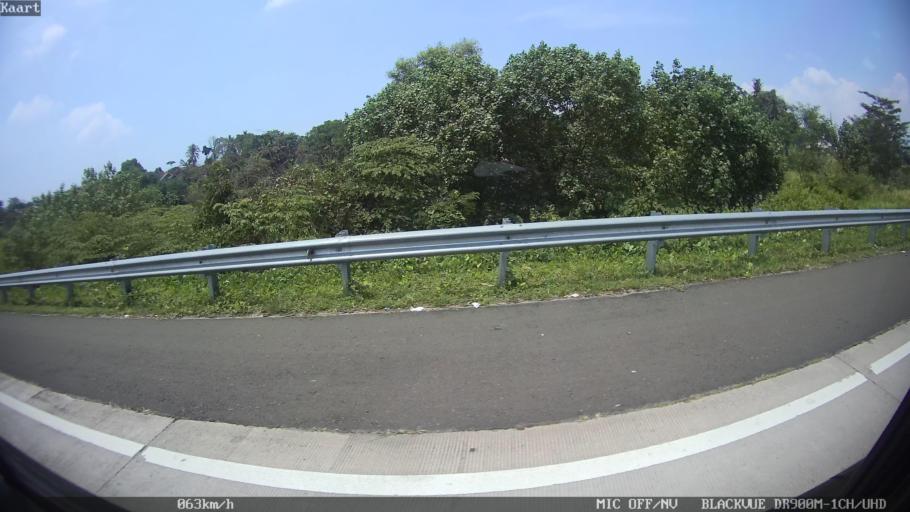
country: ID
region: Lampung
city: Kedaton
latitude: -5.3343
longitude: 105.2980
